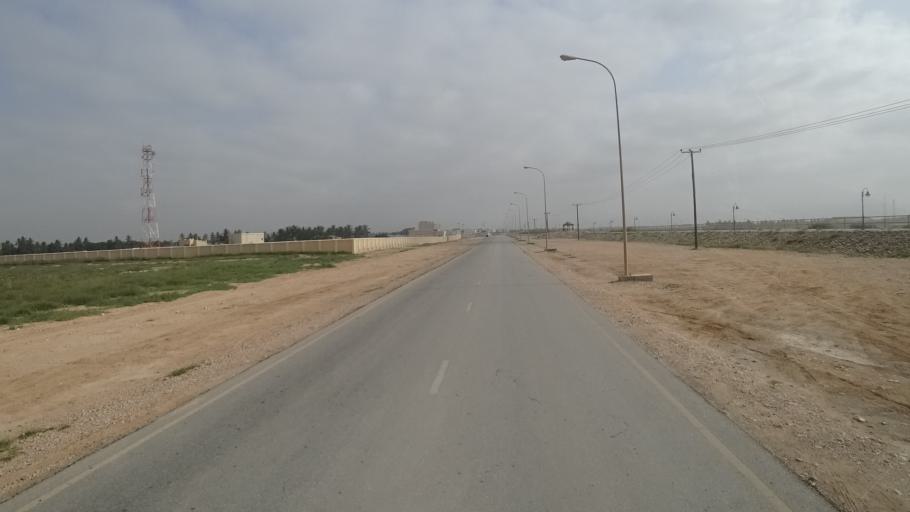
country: OM
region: Zufar
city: Salalah
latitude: 17.0179
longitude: 54.1744
